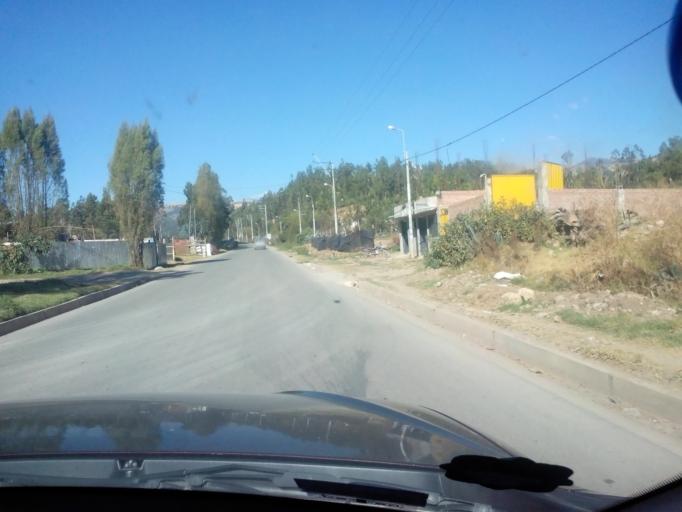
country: PE
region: Apurimac
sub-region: Provincia de Andahuaylas
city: Talavera
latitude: -13.6594
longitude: -73.4260
